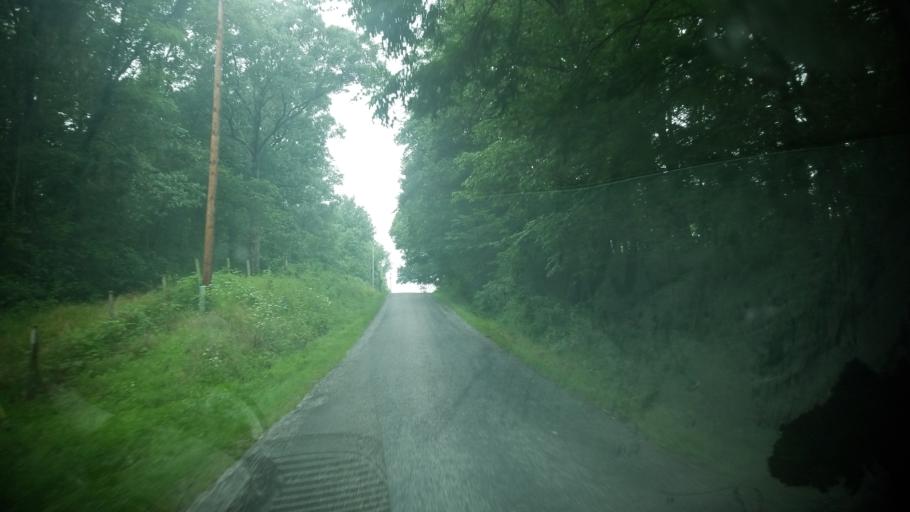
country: US
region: Illinois
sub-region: Clay County
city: Flora
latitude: 38.5735
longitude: -88.3896
